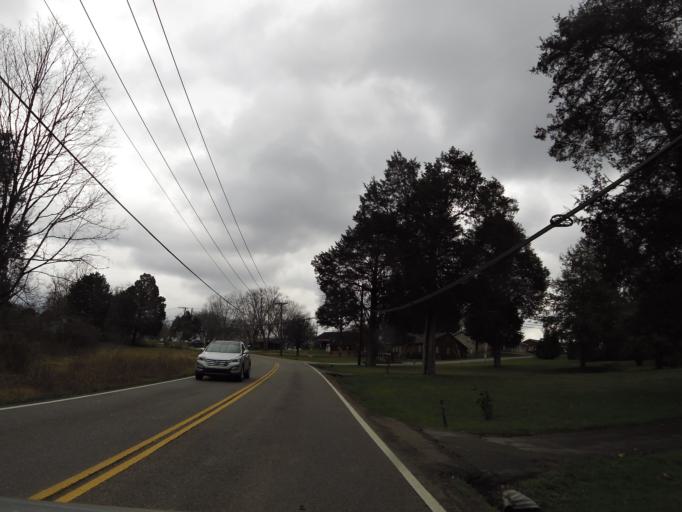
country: US
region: Tennessee
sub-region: Knox County
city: Knoxville
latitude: 36.0855
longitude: -83.9200
